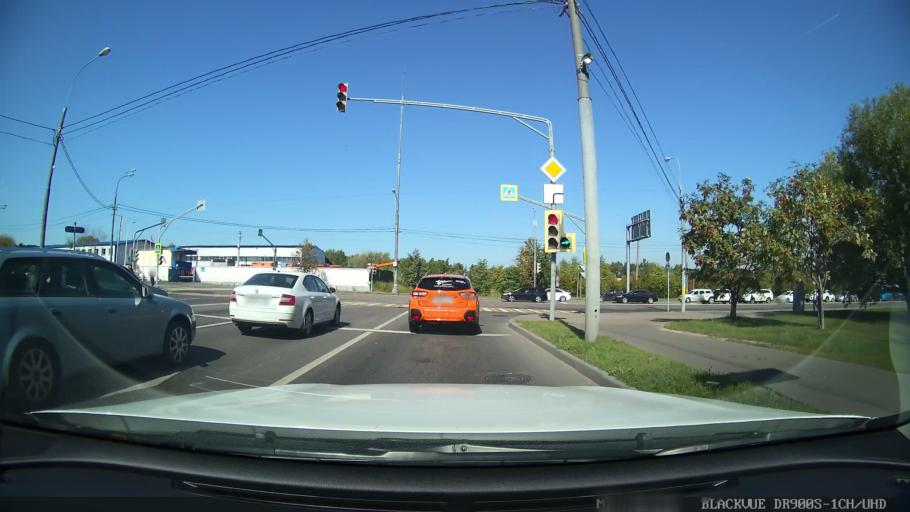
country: RU
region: Moscow
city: Strogino
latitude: 55.7712
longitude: 37.4051
